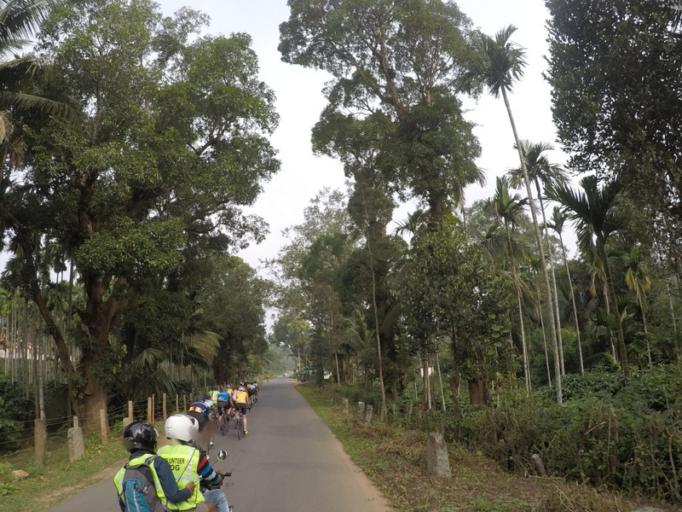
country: IN
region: Karnataka
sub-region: Chikmagalur
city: Chikmagalur
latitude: 13.3556
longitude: 75.5363
